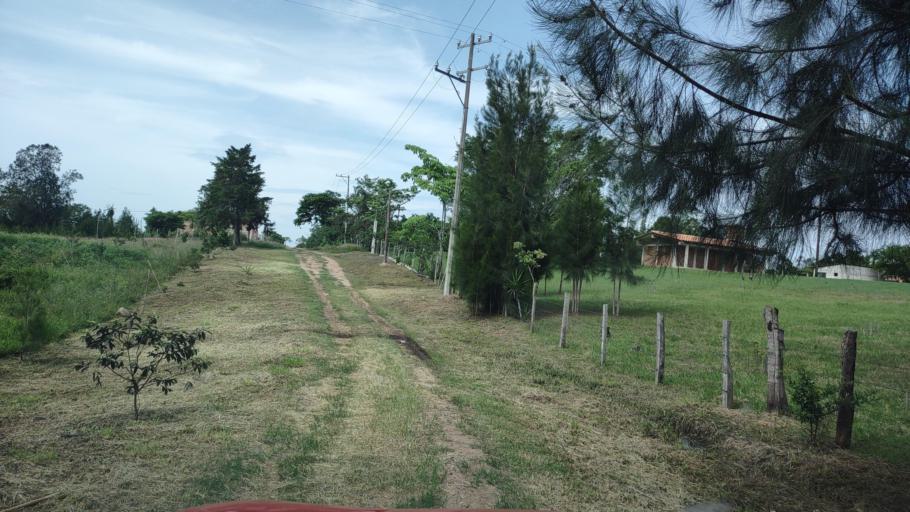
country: MX
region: Veracruz
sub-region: Emiliano Zapata
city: Dos Rios
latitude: 19.4712
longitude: -96.8268
